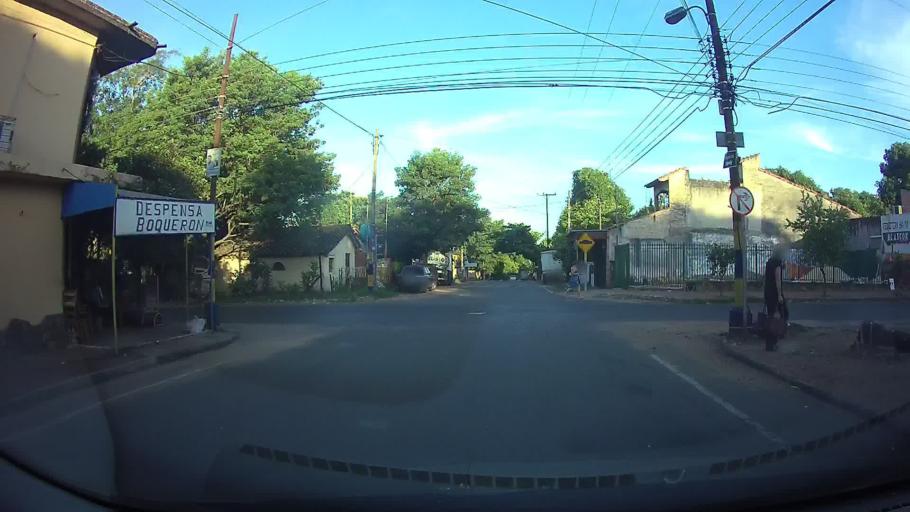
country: PY
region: Central
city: San Lorenzo
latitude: -25.2729
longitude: -57.4982
